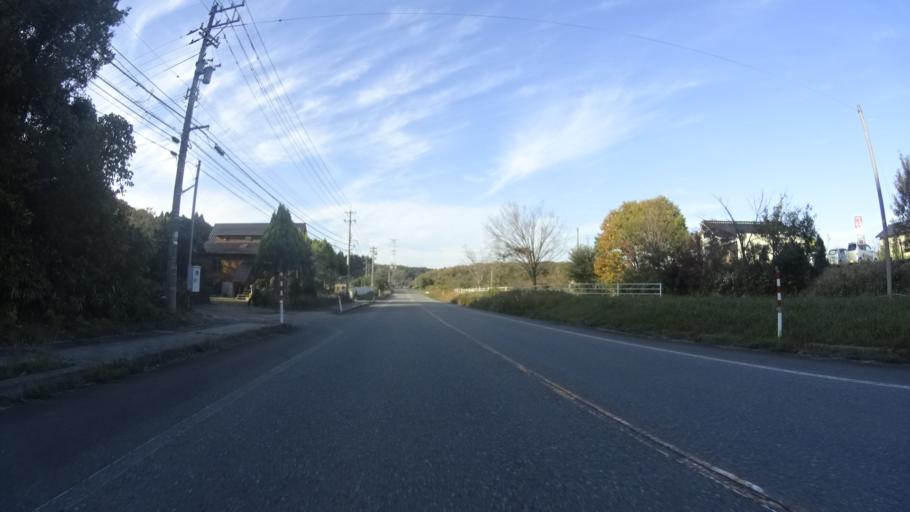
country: JP
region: Ishikawa
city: Hakui
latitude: 37.0417
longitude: 136.7773
